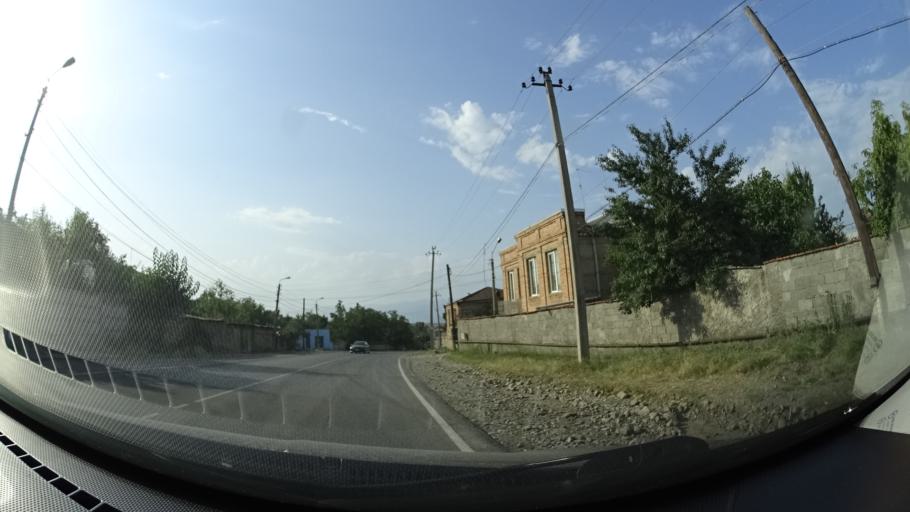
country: GE
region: Kakheti
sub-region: Gurjaani
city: Gurjaani
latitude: 41.7675
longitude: 45.7727
